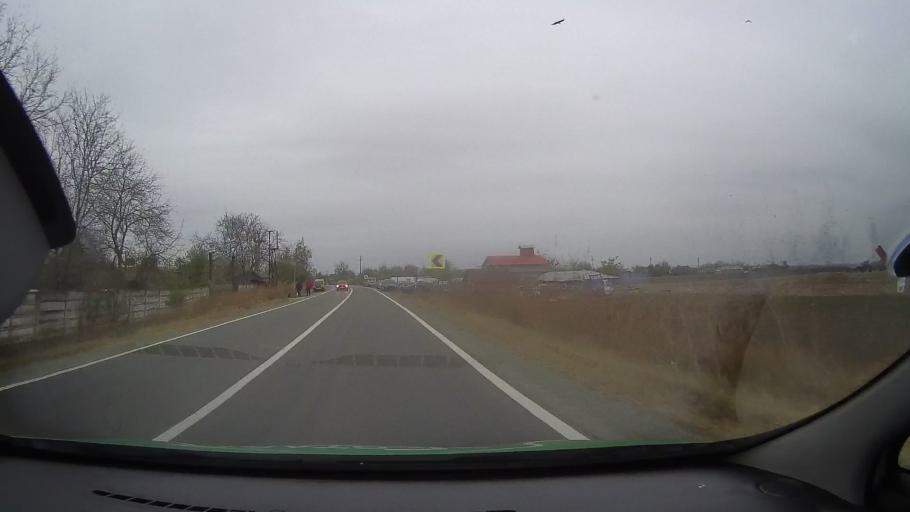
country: RO
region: Ialomita
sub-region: Comuna Slobozia
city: Slobozia
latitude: 44.6086
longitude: 27.3850
